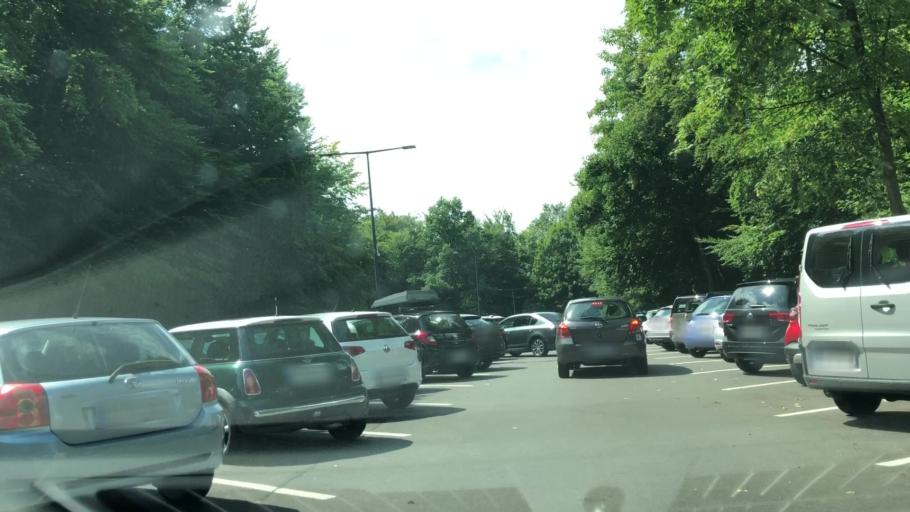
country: DE
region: North Rhine-Westphalia
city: Porta Westfalica
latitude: 52.2468
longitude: 8.9013
